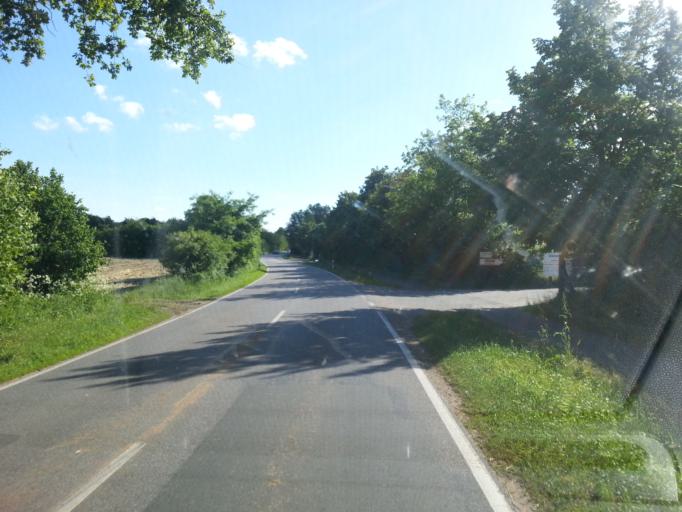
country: DE
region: Schleswig-Holstein
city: Ratekau
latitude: 53.9937
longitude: 10.7162
